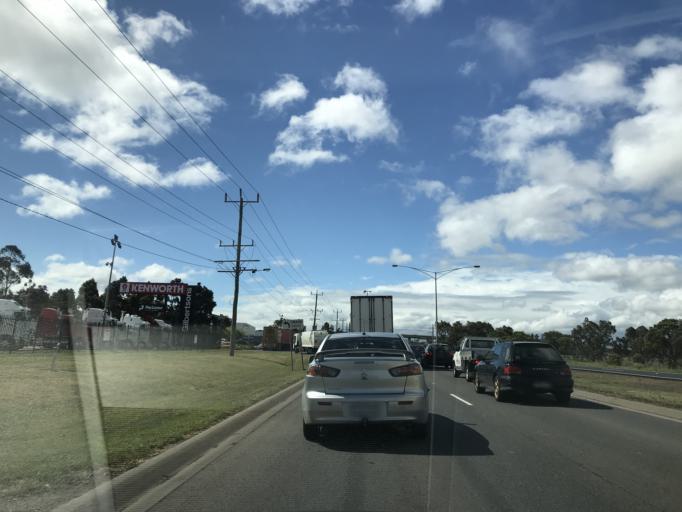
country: AU
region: Victoria
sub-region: Brimbank
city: Derrimut
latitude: -37.8066
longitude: 144.7881
